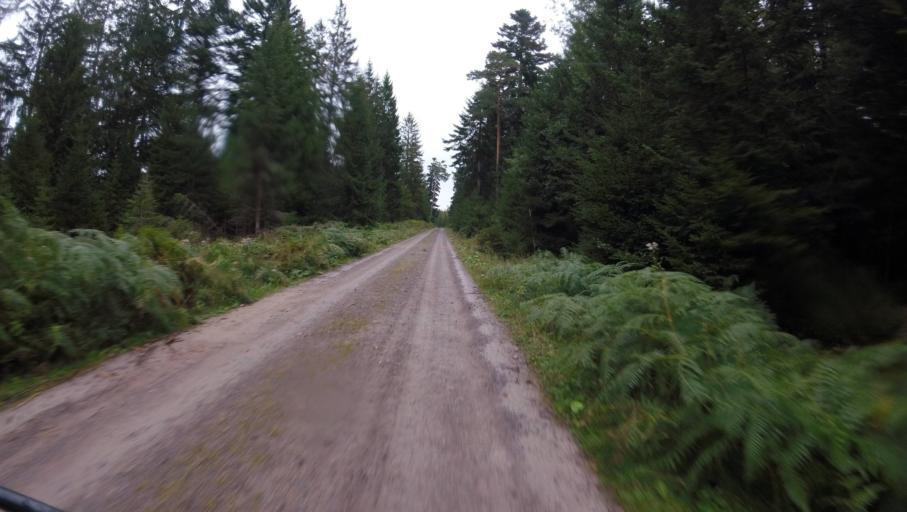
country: DE
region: Baden-Wuerttemberg
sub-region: Karlsruhe Region
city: Forbach
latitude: 48.6462
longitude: 8.3912
